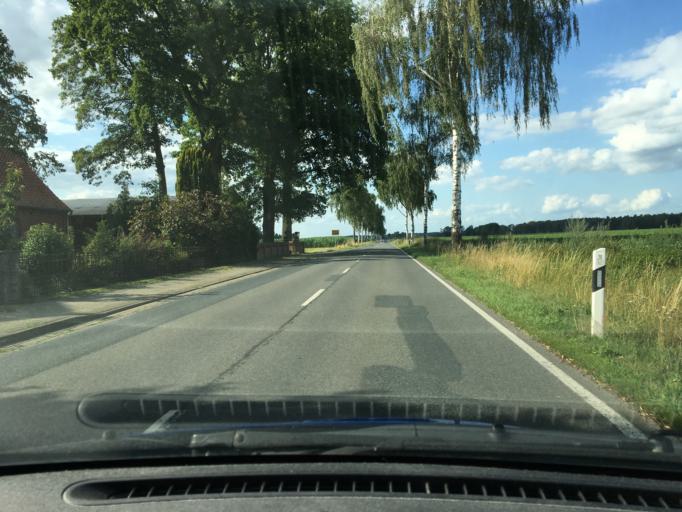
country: DE
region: Lower Saxony
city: Altenmedingen
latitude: 53.1107
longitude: 10.6001
